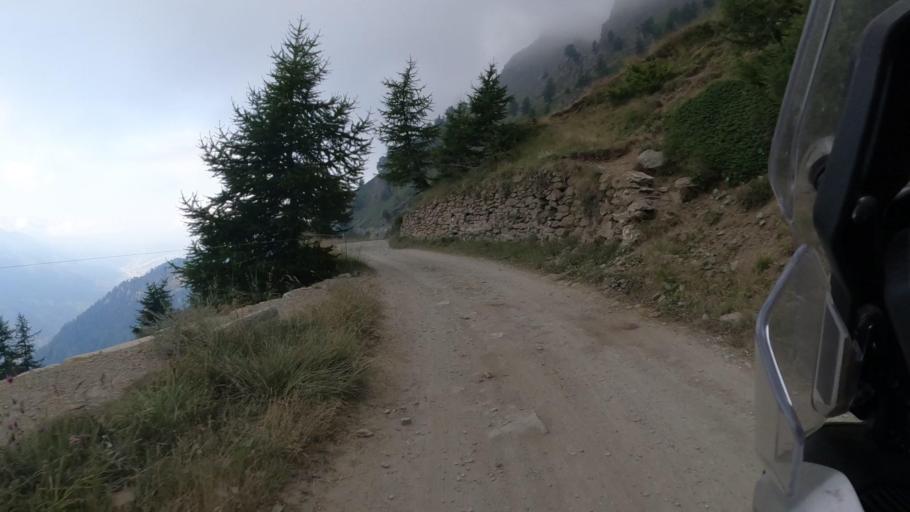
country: IT
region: Piedmont
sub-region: Provincia di Torino
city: Usseaux
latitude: 45.0621
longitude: 6.9979
